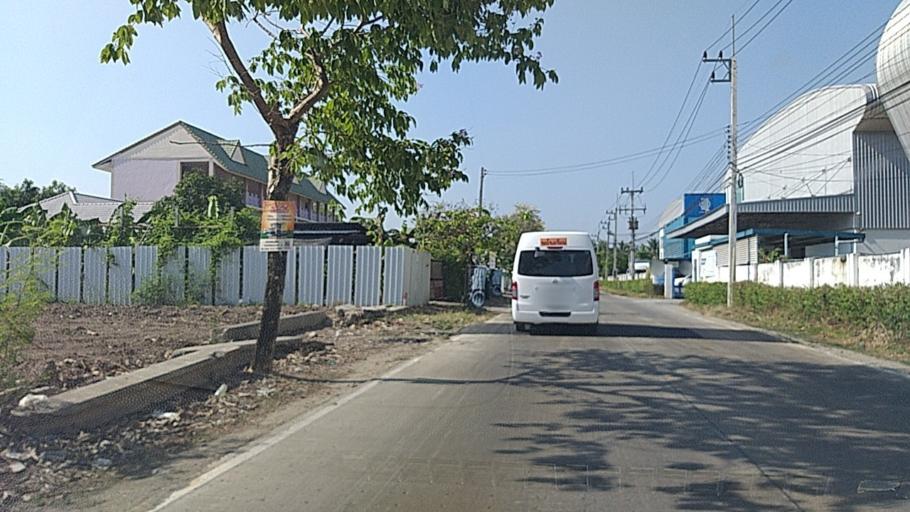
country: TH
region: Nakhon Pathom
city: Salaya
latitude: 13.8111
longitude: 100.3091
